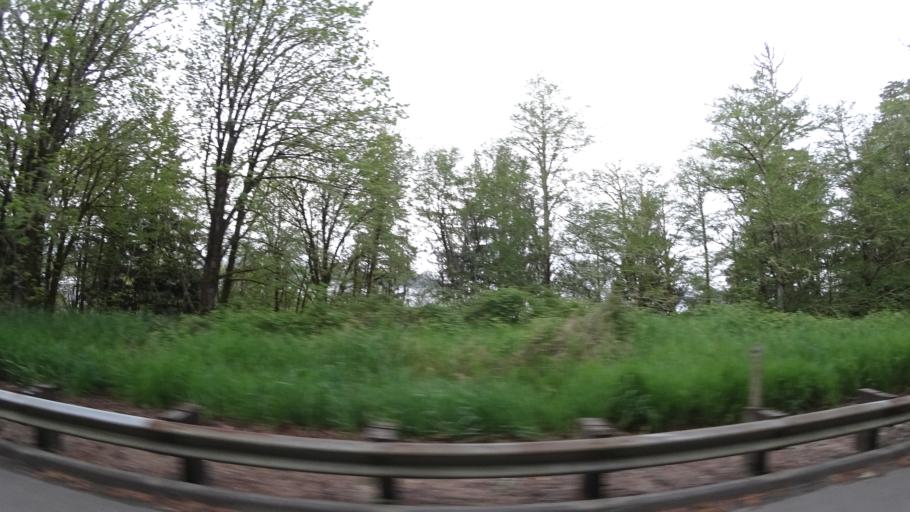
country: US
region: Oregon
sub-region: Douglas County
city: Reedsport
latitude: 43.7498
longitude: -124.1214
